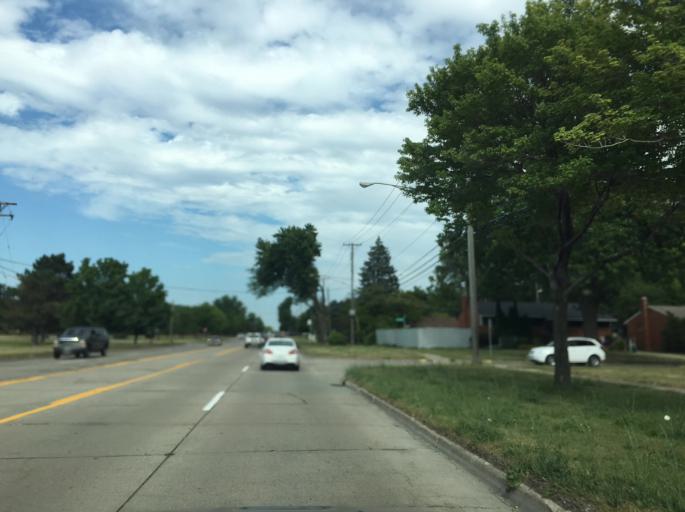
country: US
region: Michigan
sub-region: Macomb County
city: Sterling Heights
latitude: 42.5358
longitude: -83.0576
